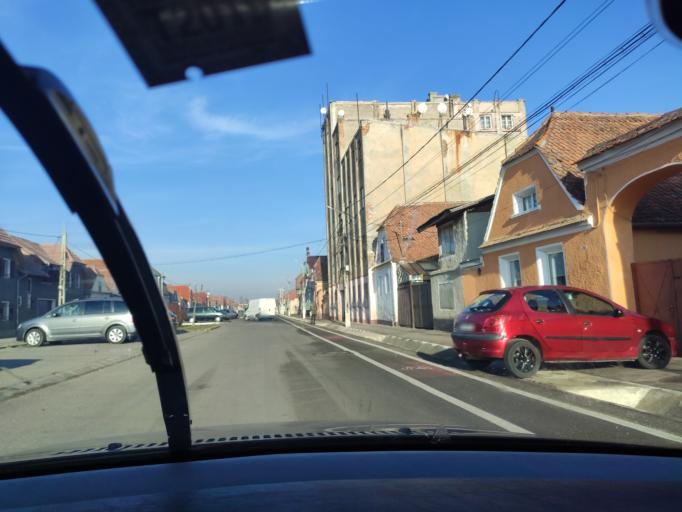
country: RO
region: Brasov
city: Codlea
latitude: 45.6988
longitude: 25.4497
